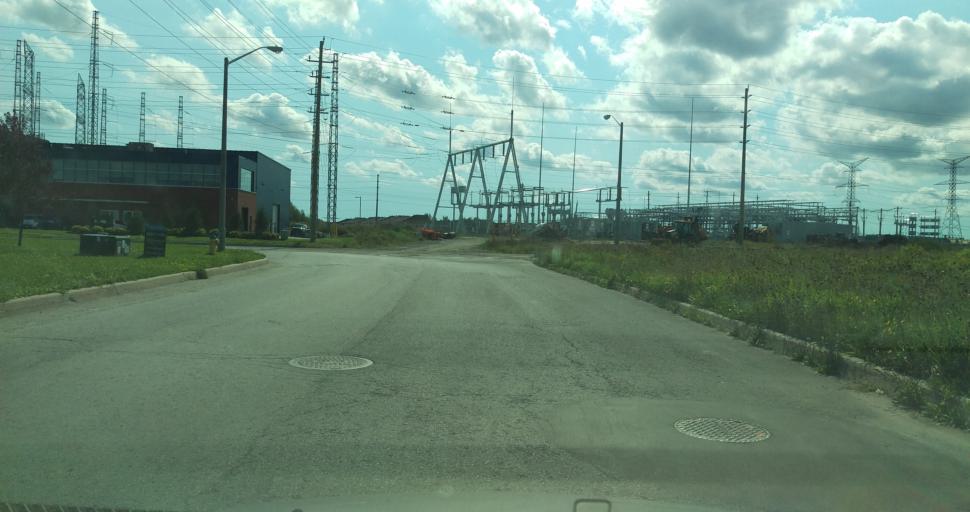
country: CA
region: Quebec
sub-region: Outaouais
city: Gatineau
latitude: 45.4566
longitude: -75.4917
